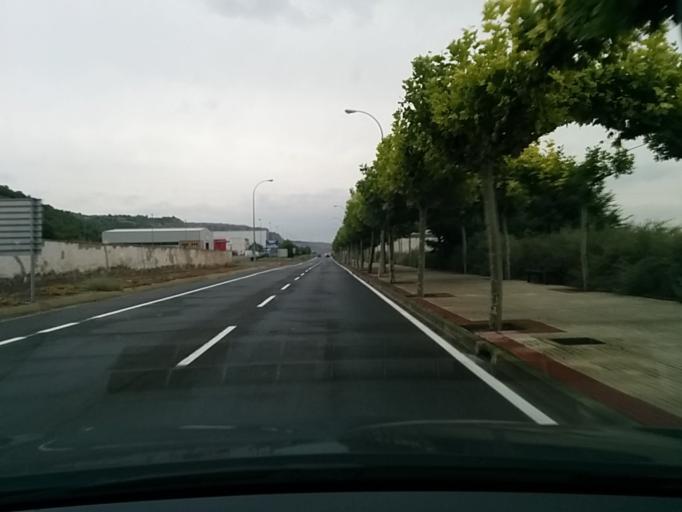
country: ES
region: Navarre
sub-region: Provincia de Navarra
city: Valtierra
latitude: 42.1891
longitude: -1.6241
